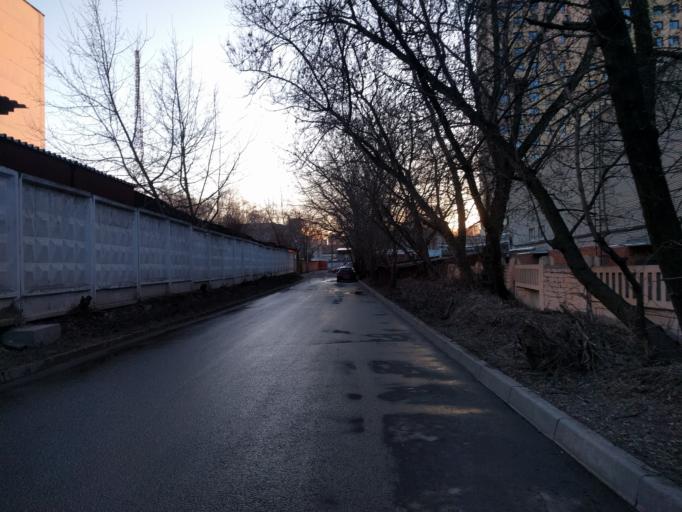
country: RU
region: Moscow
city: Sokol
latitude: 55.7844
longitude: 37.4988
